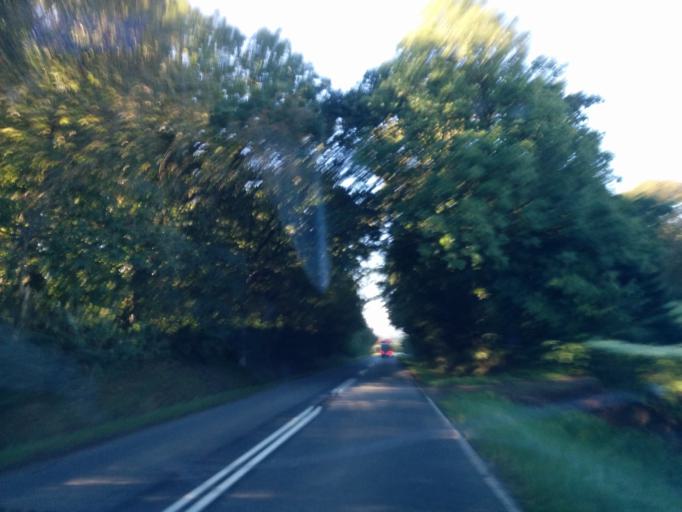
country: DK
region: South Denmark
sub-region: Kolding Kommune
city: Sonder Bjert
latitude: 55.4114
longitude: 9.5584
